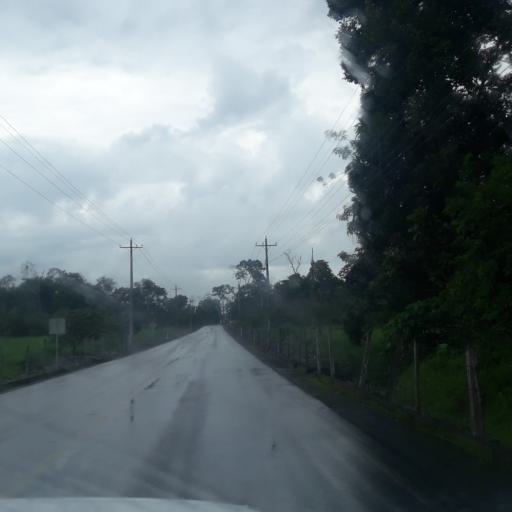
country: EC
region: Napo
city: Tena
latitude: -1.0667
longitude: -77.6505
